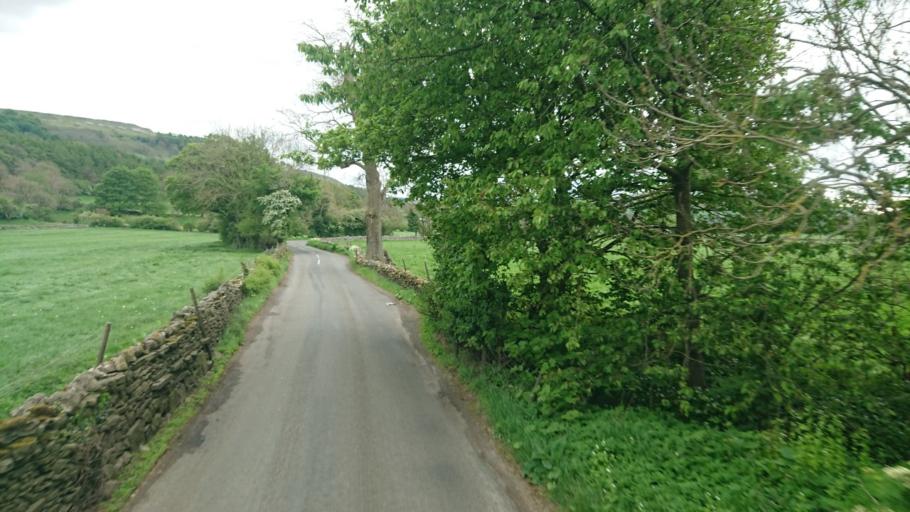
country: GB
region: England
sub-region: North Yorkshire
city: Leyburn
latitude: 54.2901
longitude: -1.9661
